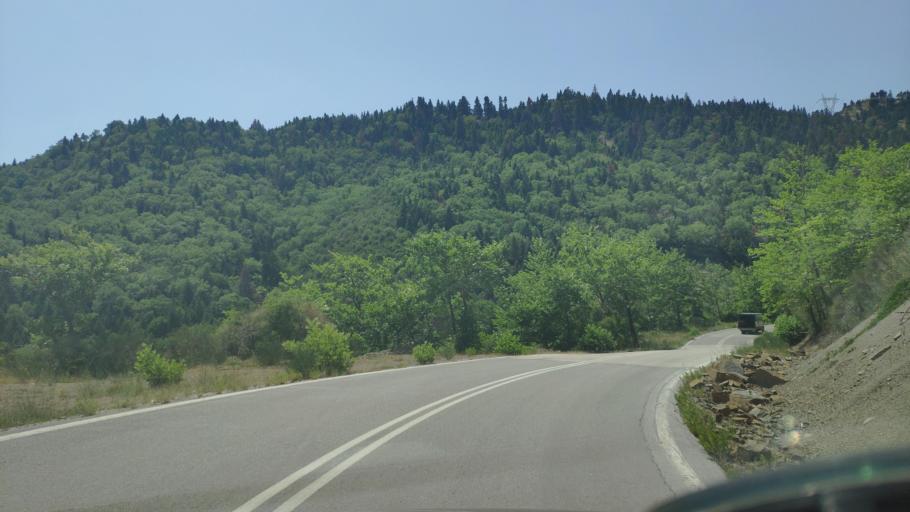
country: GR
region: Thessaly
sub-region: Nomos Kardhitsas
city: Anthiro
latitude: 39.2703
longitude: 21.3518
